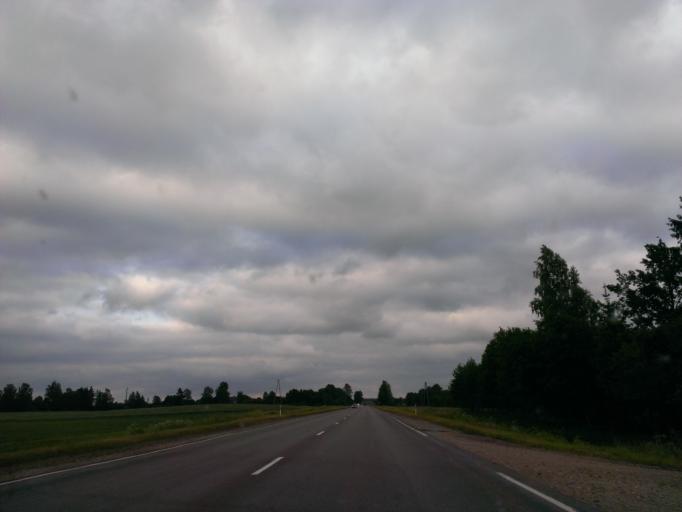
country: LV
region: Saldus Rajons
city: Saldus
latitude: 56.6688
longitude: 22.3177
